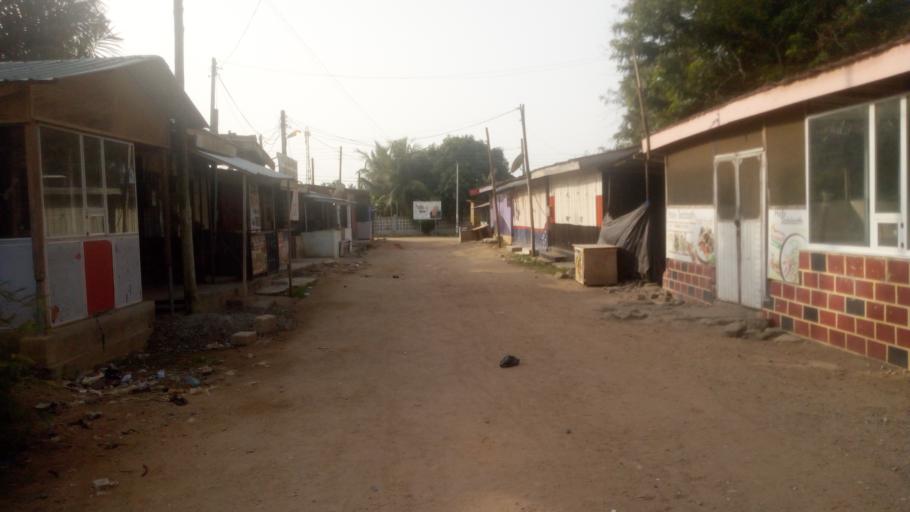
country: GH
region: Central
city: Winneba
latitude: 5.3597
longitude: -0.6310
